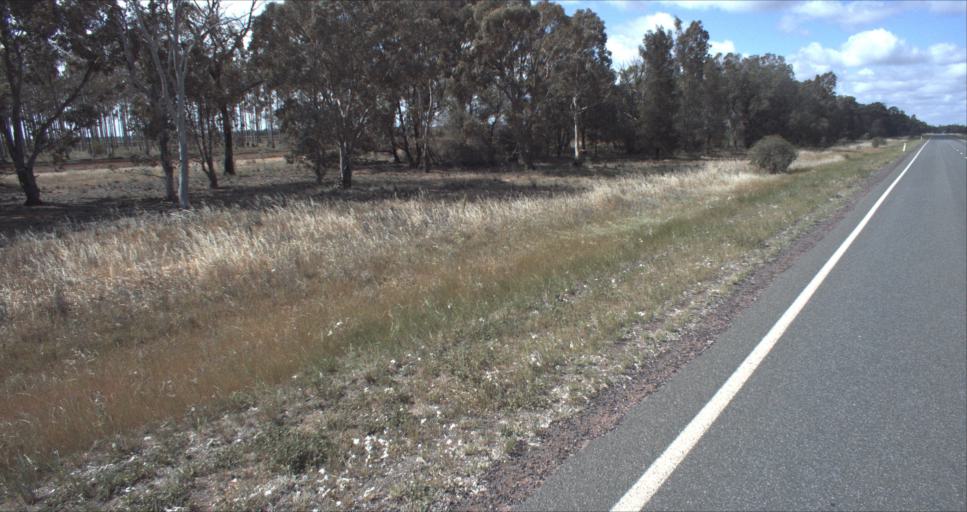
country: AU
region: New South Wales
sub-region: Murrumbidgee Shire
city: Darlington Point
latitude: -34.5857
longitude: 146.1643
